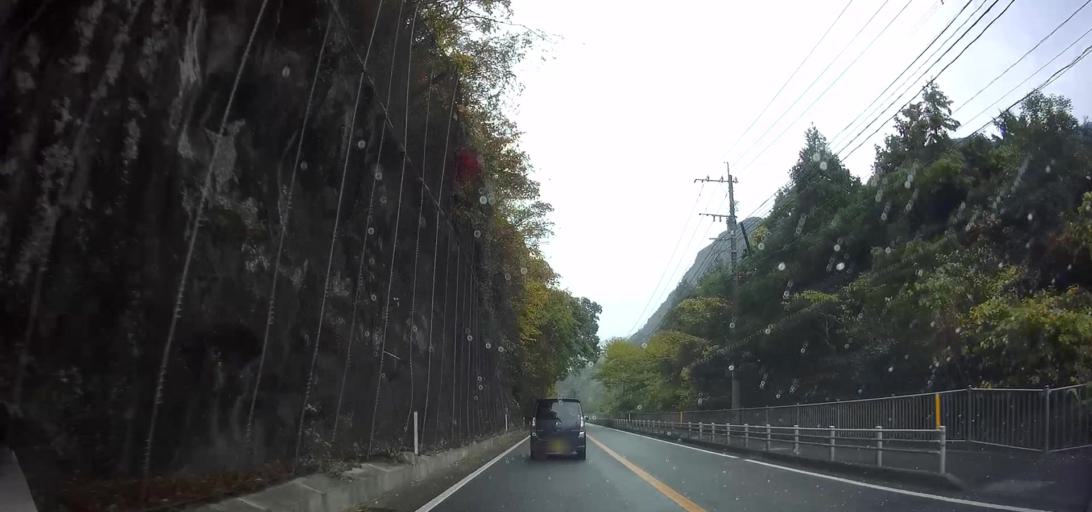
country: JP
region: Nagasaki
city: Shimabara
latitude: 32.7734
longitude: 130.2138
